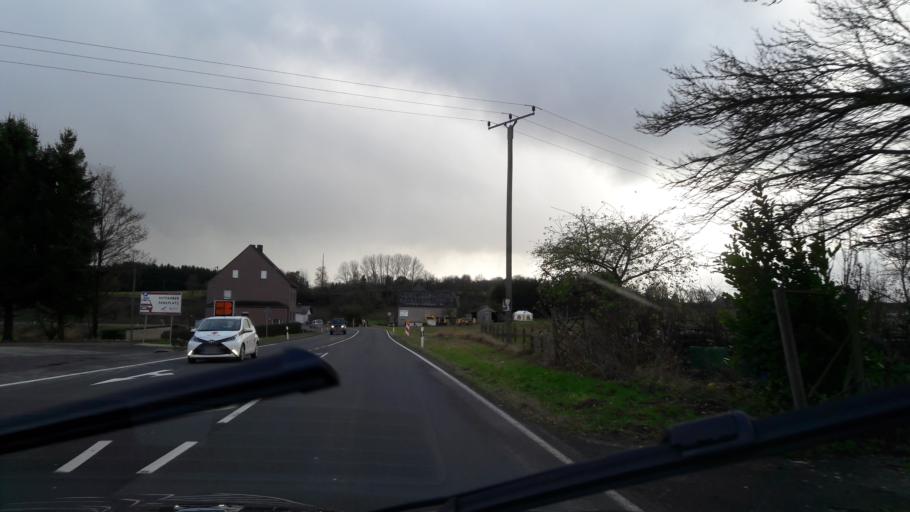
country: DE
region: Rheinland-Pfalz
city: Reinsfeld
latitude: 49.6711
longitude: 6.9014
